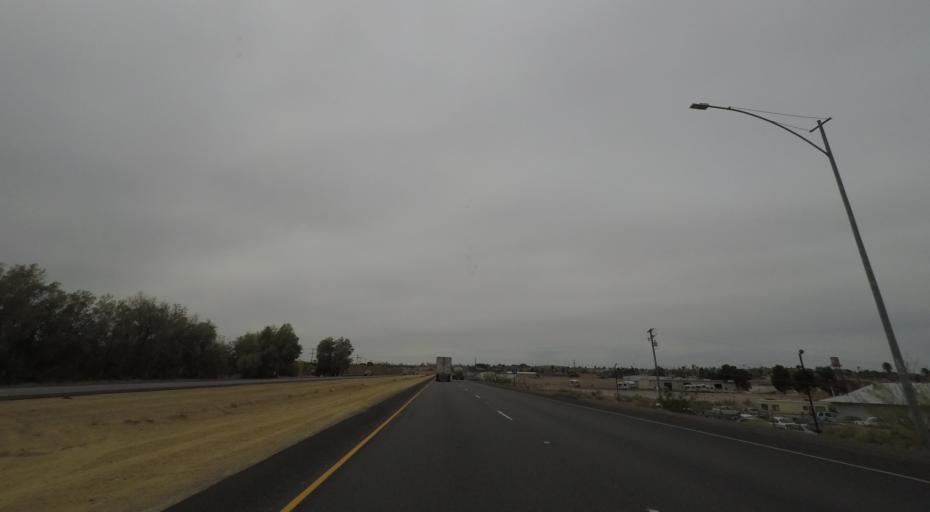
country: US
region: California
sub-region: San Bernardino County
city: Barstow
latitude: 34.8868
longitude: -116.9980
